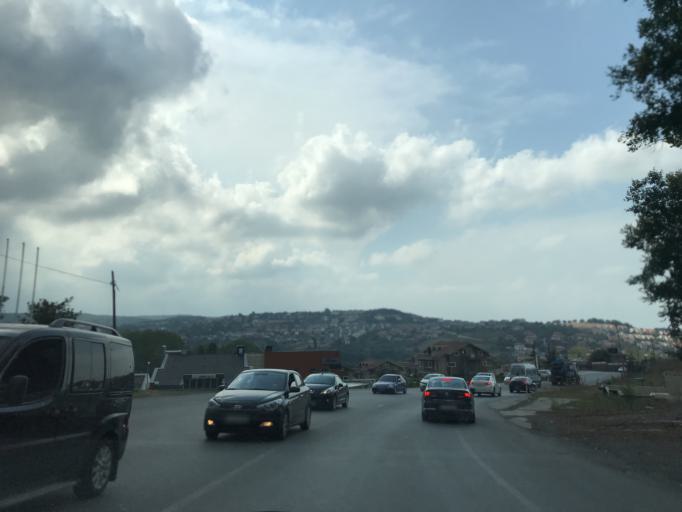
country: TR
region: Istanbul
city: Arikoey
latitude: 41.2108
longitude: 29.0381
